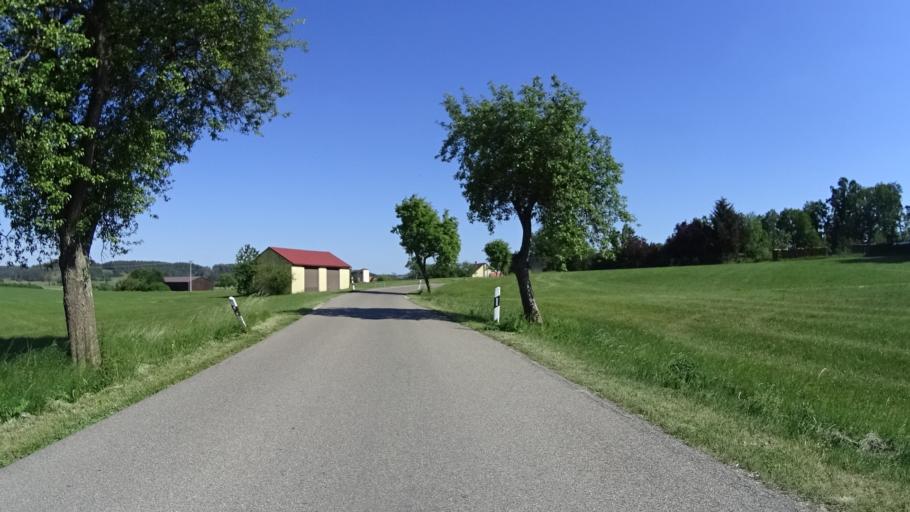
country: DE
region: Bavaria
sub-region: Regierungsbezirk Mittelfranken
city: Dombuhl
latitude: 49.2208
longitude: 10.3021
